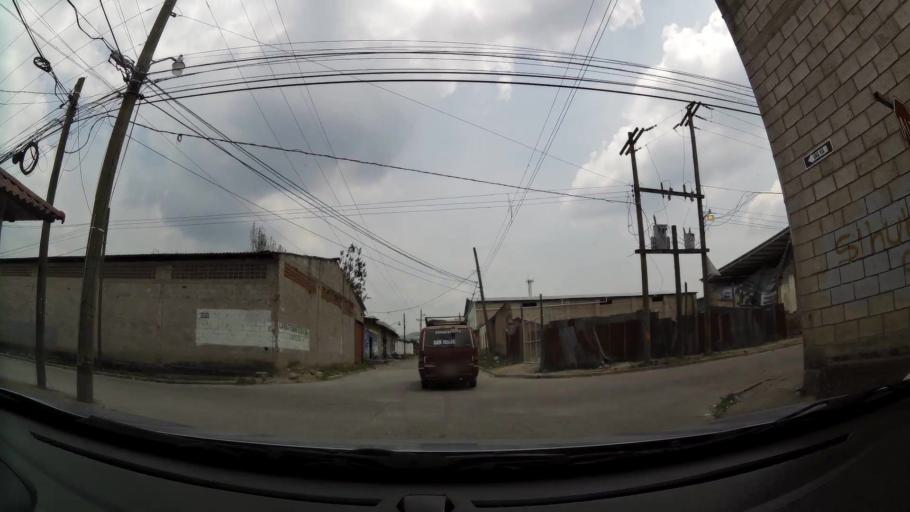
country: HN
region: Comayagua
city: Siguatepeque
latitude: 14.6026
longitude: -87.8318
